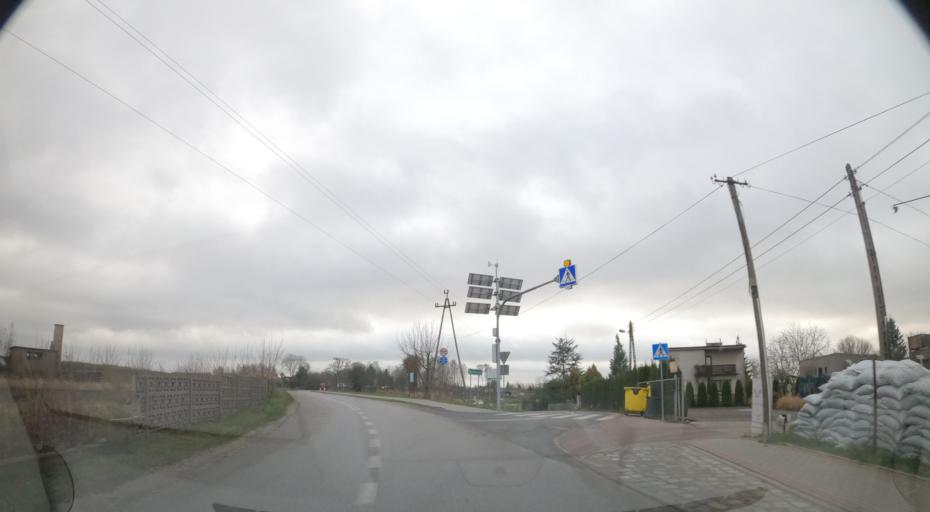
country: PL
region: Greater Poland Voivodeship
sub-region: Powiat pilski
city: Lobzenica
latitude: 53.2587
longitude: 17.2613
